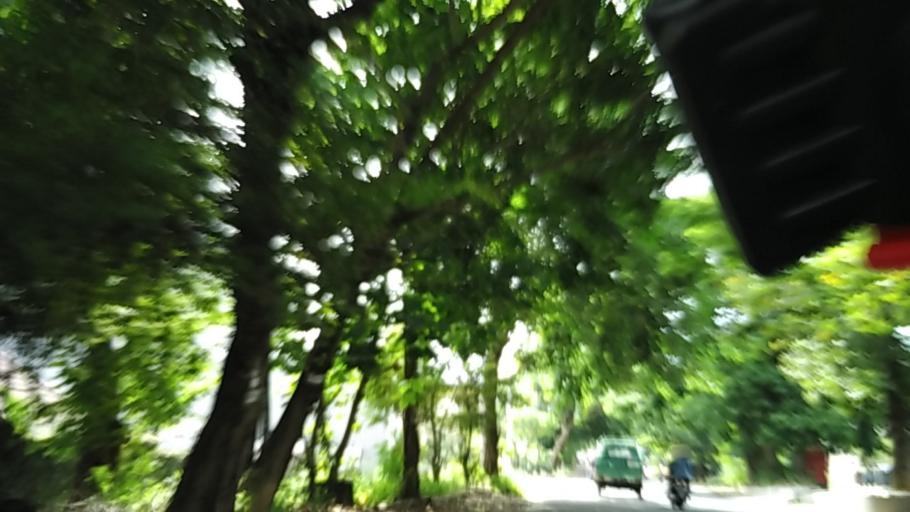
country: ID
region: Central Java
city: Semarang
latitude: -7.0091
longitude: 110.4222
